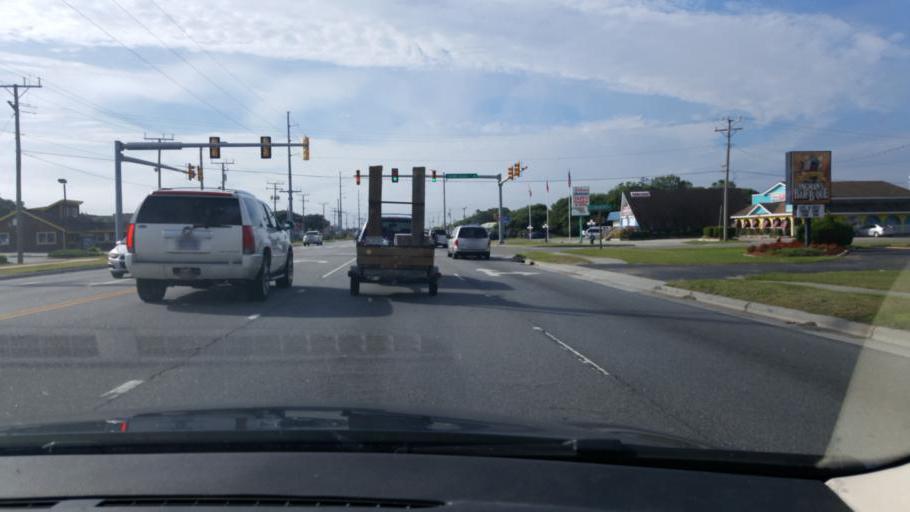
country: US
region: North Carolina
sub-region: Dare County
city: Kill Devil Hills
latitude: 35.9982
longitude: -75.6517
